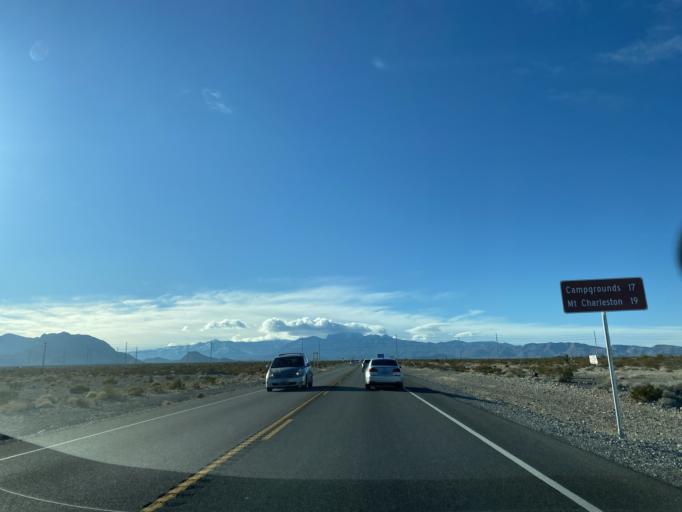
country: US
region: Nevada
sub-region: Clark County
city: Summerlin South
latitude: 36.3262
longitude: -115.3199
